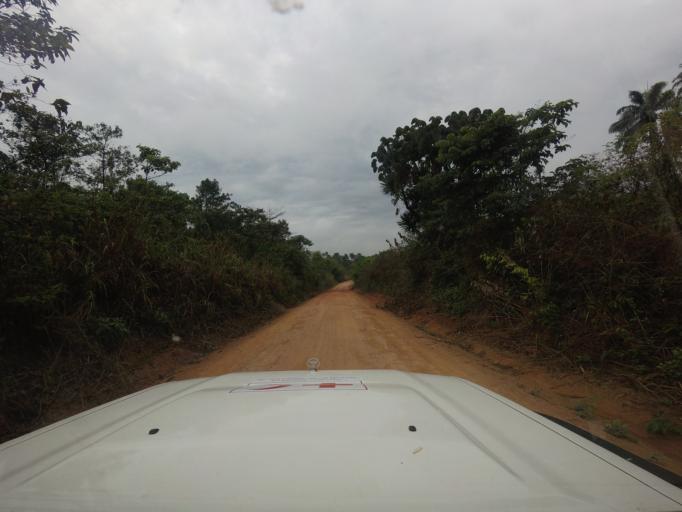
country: SL
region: Eastern Province
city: Buedu
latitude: 8.2864
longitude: -10.1237
